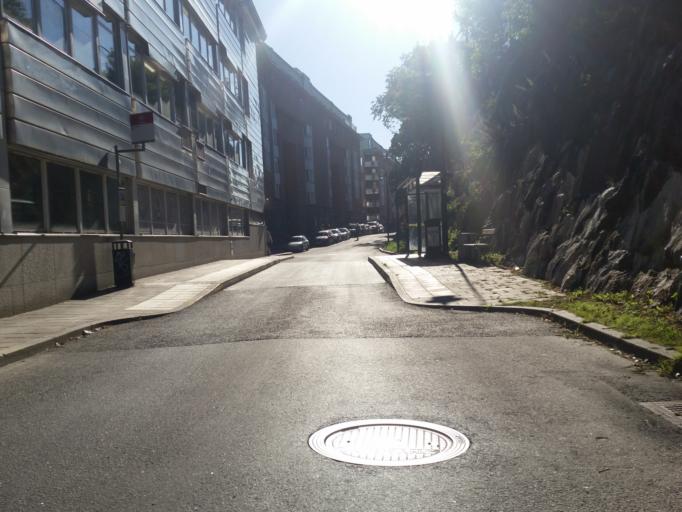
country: SE
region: Stockholm
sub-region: Stockholms Kommun
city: OEstermalm
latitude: 59.3061
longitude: 18.0864
